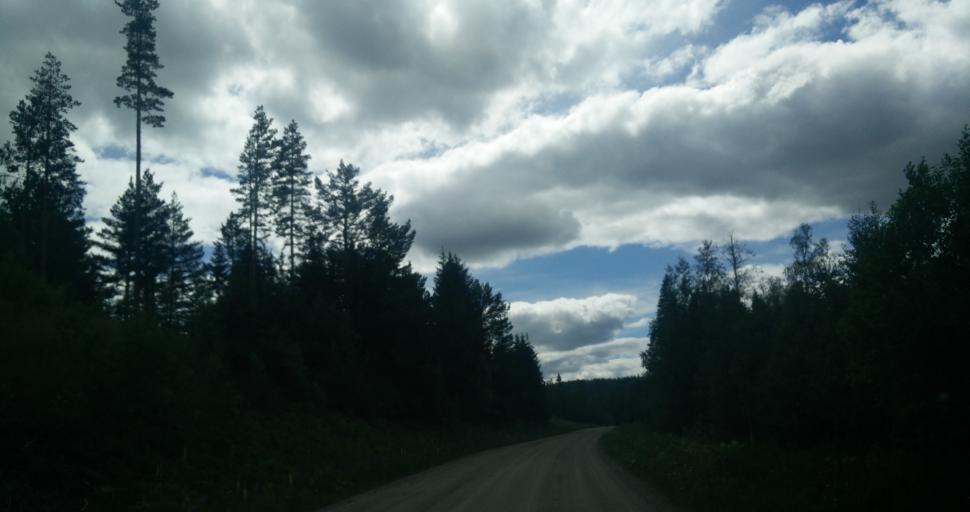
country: SE
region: Gaevleborg
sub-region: Nordanstigs Kommun
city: Bergsjoe
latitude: 62.1192
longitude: 17.1008
